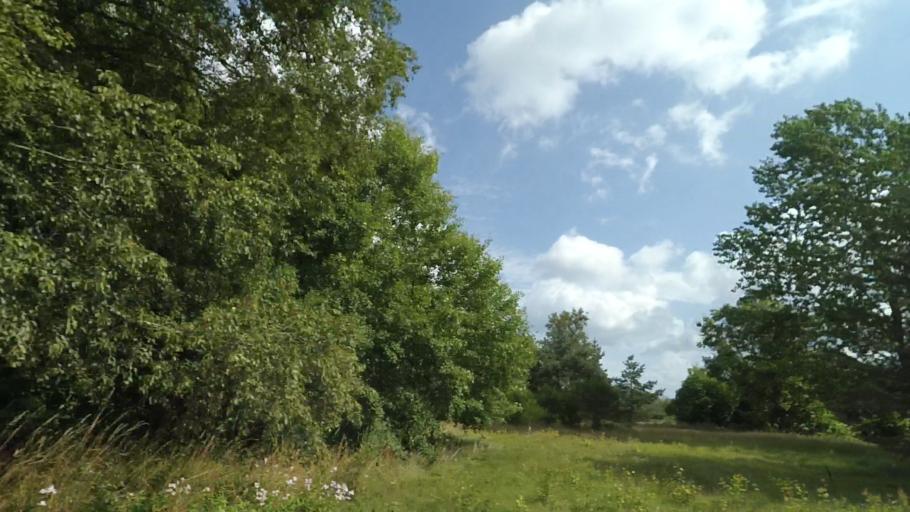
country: DK
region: Central Jutland
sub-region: Norddjurs Kommune
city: Allingabro
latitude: 56.5128
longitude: 10.4006
